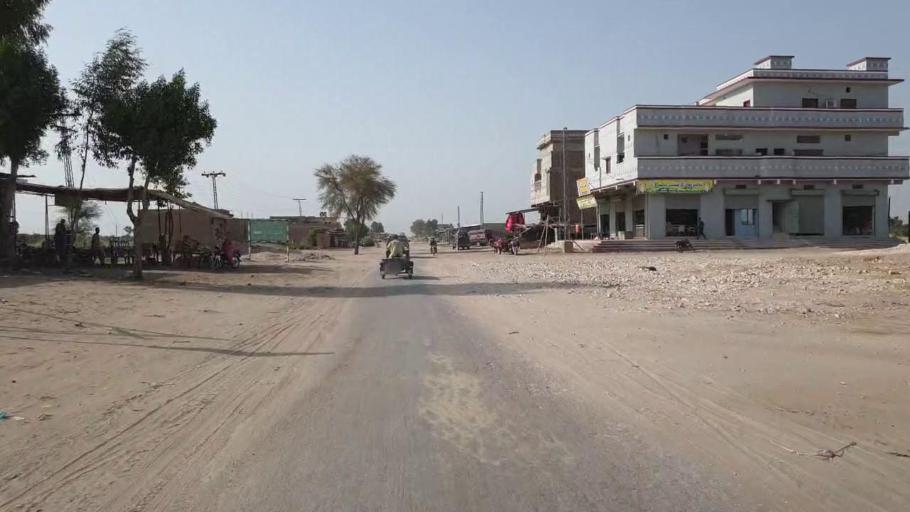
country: PK
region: Sindh
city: Sanghar
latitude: 26.2754
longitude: 68.9301
